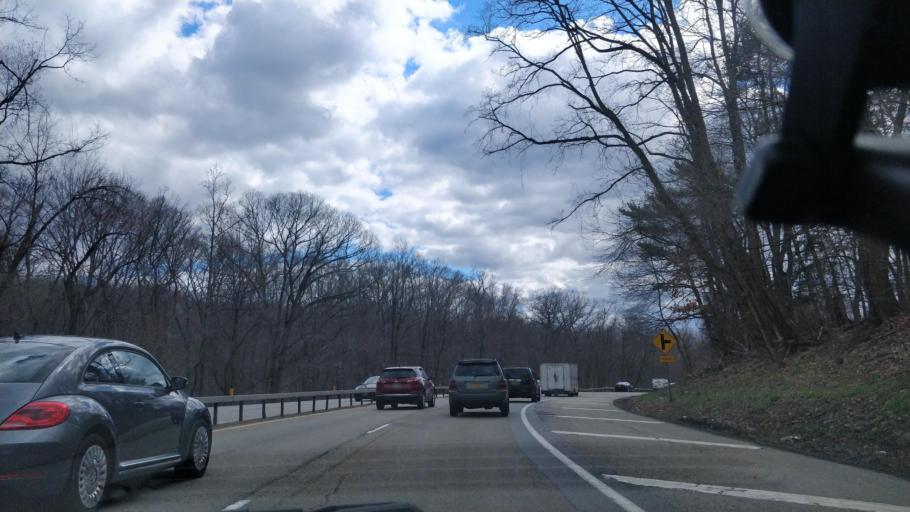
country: US
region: New York
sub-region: Westchester County
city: Ossining
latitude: 41.1802
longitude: -73.8392
